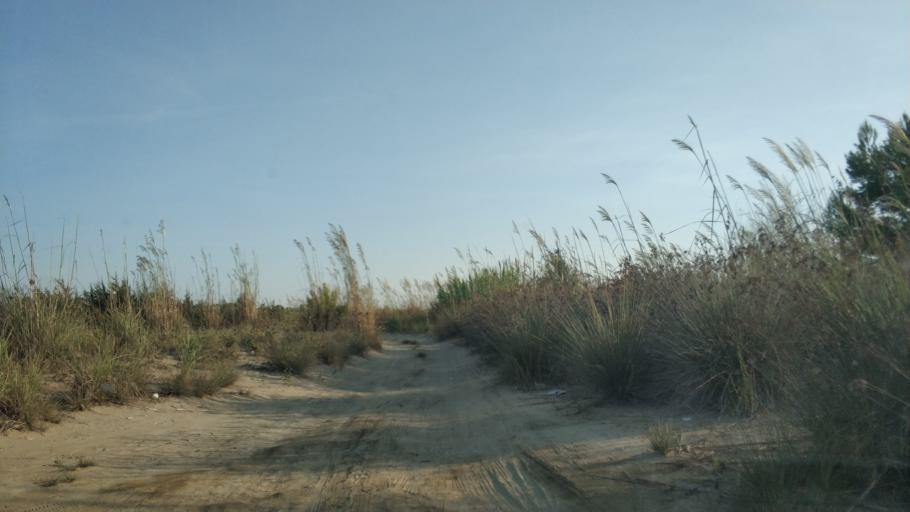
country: AL
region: Fier
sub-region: Rrethi i Lushnjes
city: Divjake
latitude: 40.9554
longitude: 19.4711
